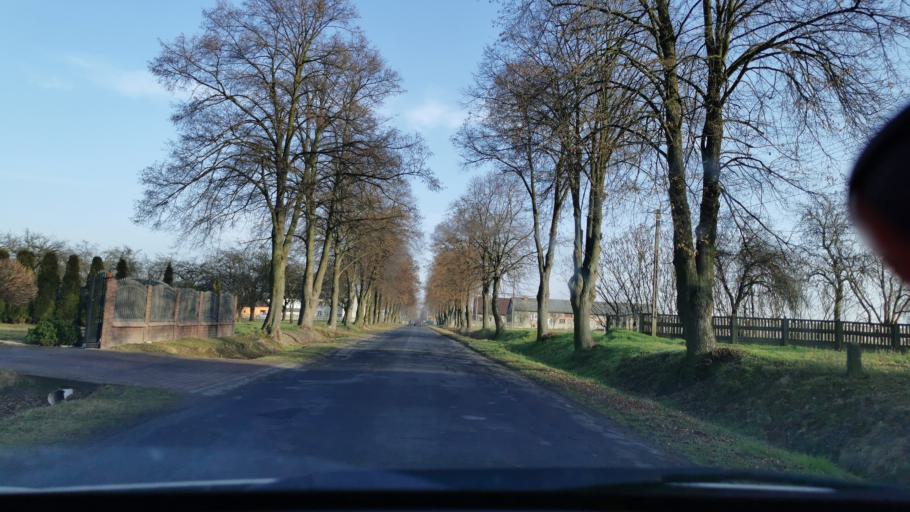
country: PL
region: Greater Poland Voivodeship
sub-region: Powiat kaliski
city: Kozminek
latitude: 51.6851
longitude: 18.3226
